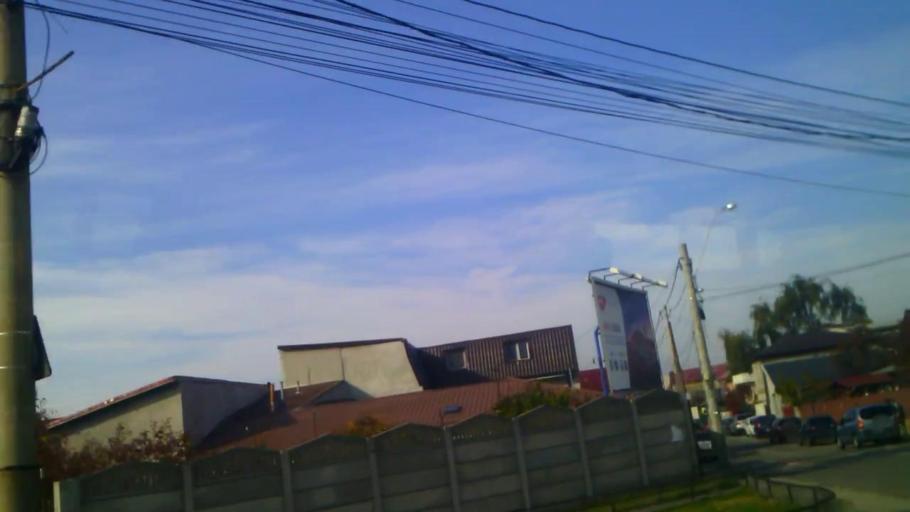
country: RO
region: Ilfov
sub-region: Comuna Popesti-Leordeni
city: Popesti-Leordeni
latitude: 44.3748
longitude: 26.1385
